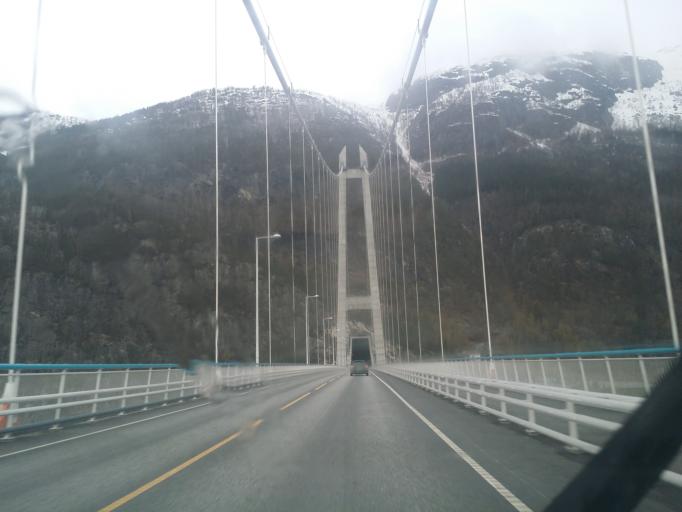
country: NO
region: Hordaland
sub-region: Granvin
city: Granvin
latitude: 60.4805
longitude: 6.8277
